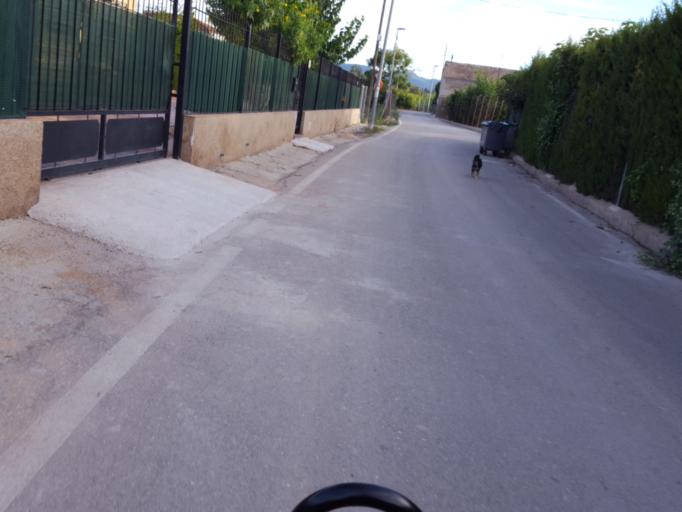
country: ES
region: Murcia
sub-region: Murcia
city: Murcia
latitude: 37.9912
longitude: -1.1692
